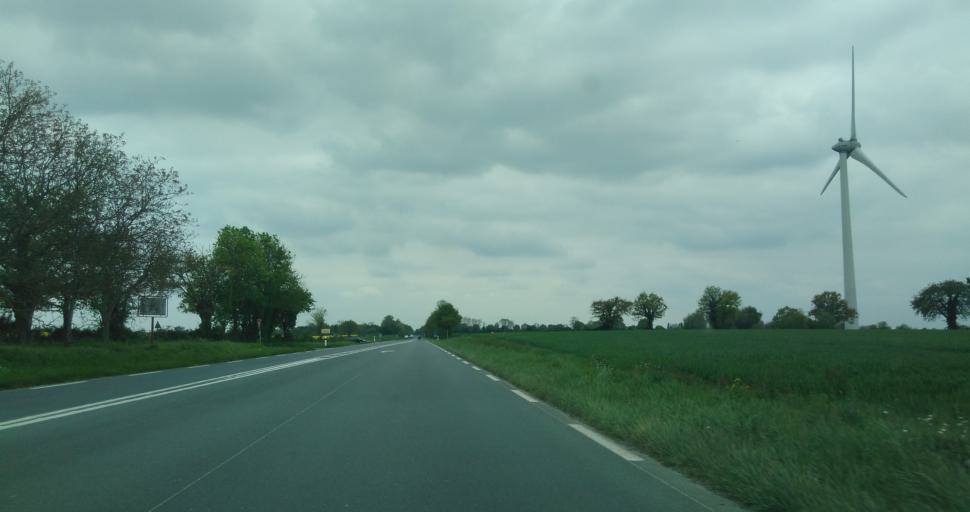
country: FR
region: Poitou-Charentes
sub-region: Departement des Deux-Sevres
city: Champdeniers-Saint-Denis
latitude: 46.4567
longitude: -0.3792
